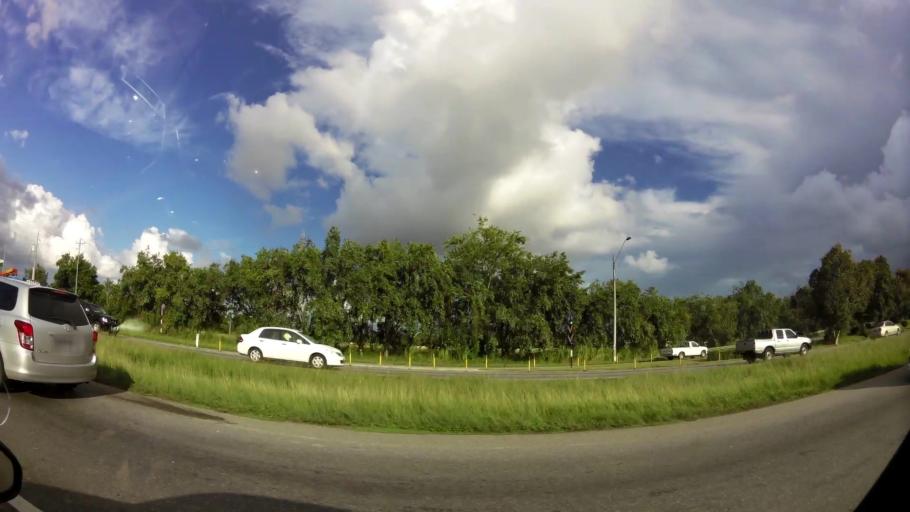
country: TT
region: Chaguanas
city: Chaguanas
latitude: 10.4847
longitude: -61.4056
